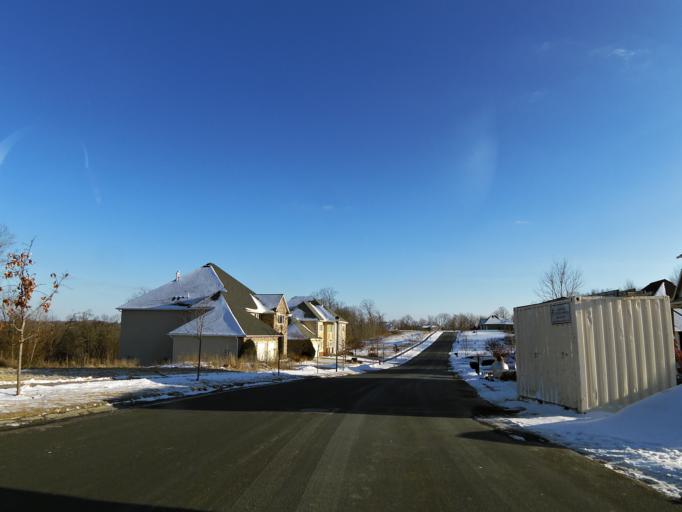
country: US
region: Minnesota
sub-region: Scott County
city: Prior Lake
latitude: 44.7406
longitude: -93.4523
